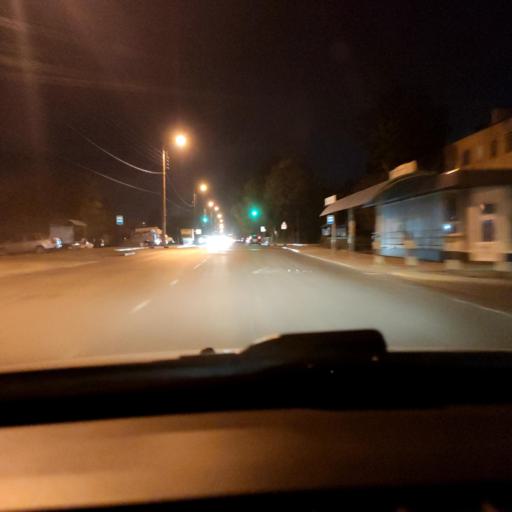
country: RU
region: Voronezj
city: Voronezh
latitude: 51.6275
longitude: 39.1761
